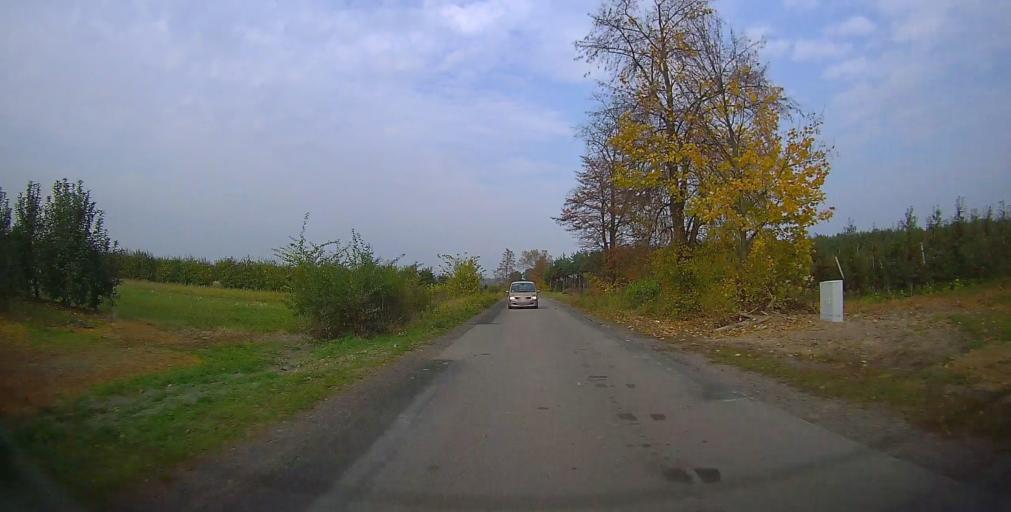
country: PL
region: Masovian Voivodeship
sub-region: Powiat grojecki
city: Mogielnica
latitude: 51.6528
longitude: 20.7236
